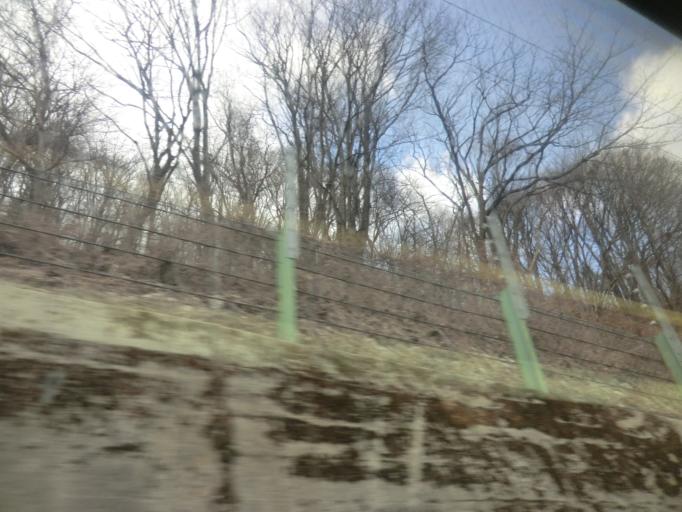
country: JP
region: Nagano
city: Ina
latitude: 35.9250
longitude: 137.7786
